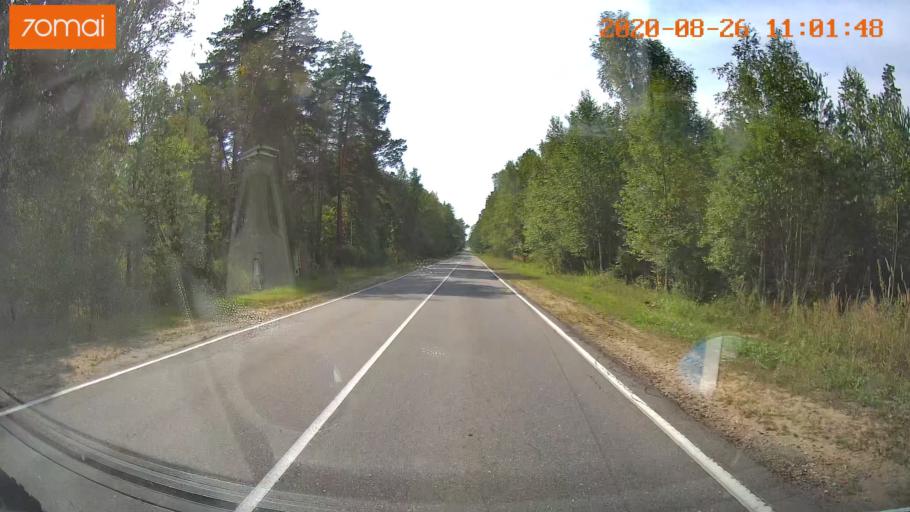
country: RU
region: Rjazan
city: Izhevskoye
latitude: 54.5590
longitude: 41.2276
